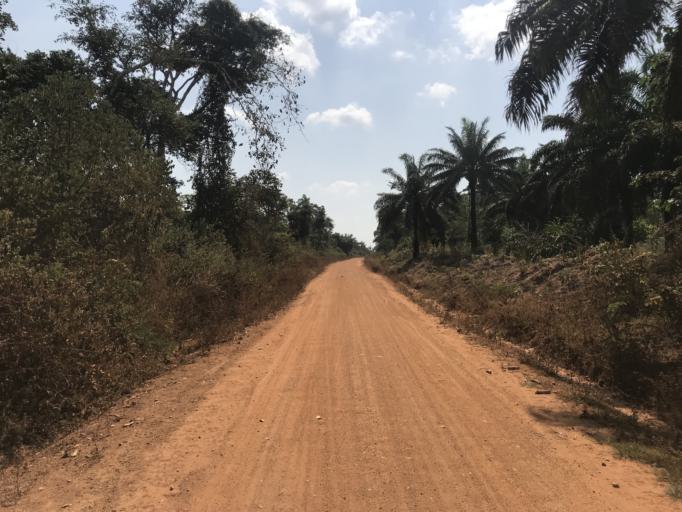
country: NG
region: Osun
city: Ifon
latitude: 7.9179
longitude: 4.4831
